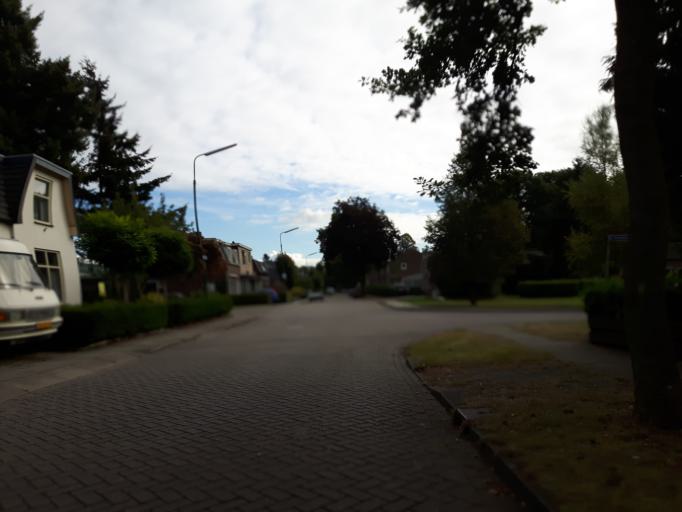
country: NL
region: Utrecht
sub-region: Gemeente Utrechtse Heuvelrug
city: Maarn
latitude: 52.0632
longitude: 5.3703
